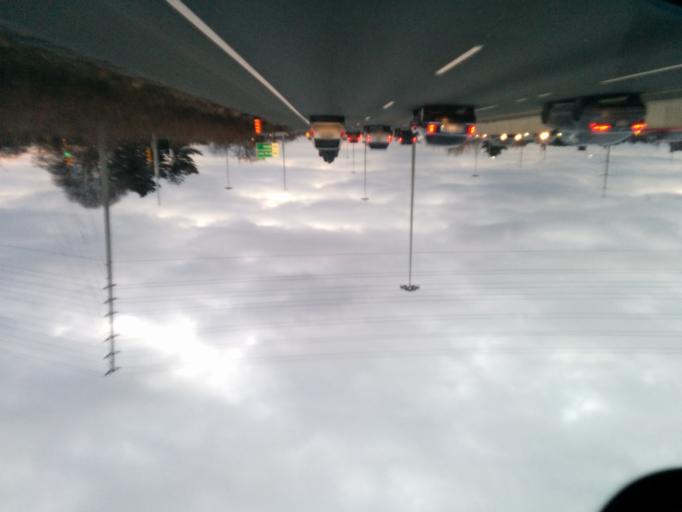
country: CA
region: Ontario
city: Mississauga
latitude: 43.5669
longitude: -79.6011
